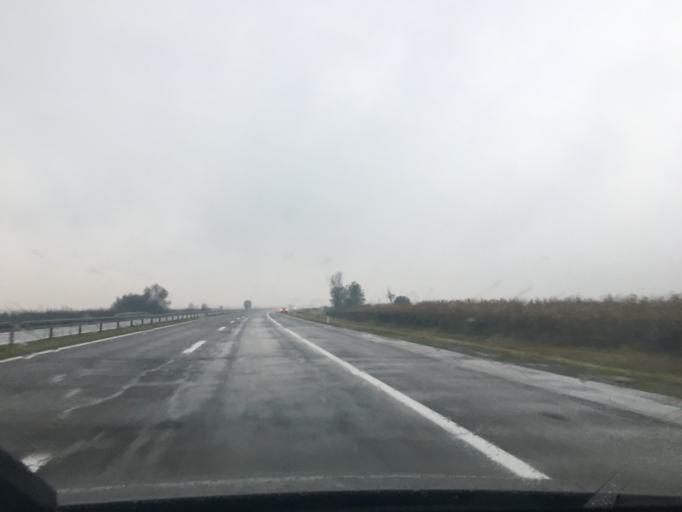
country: RS
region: Central Serbia
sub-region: Nisavski Okrug
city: Doljevac
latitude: 43.1182
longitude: 21.9173
